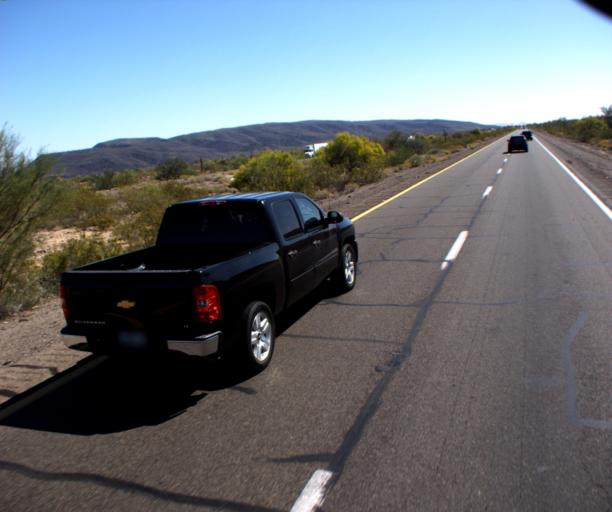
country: US
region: Arizona
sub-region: La Paz County
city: Quartzsite
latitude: 33.6558
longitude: -113.9640
